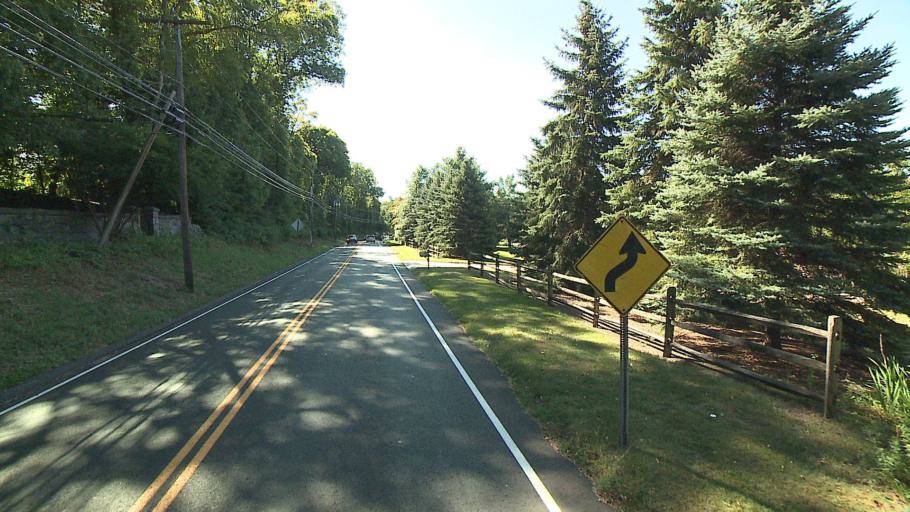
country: US
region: Connecticut
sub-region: Fairfield County
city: Darien
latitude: 41.1022
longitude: -73.4829
